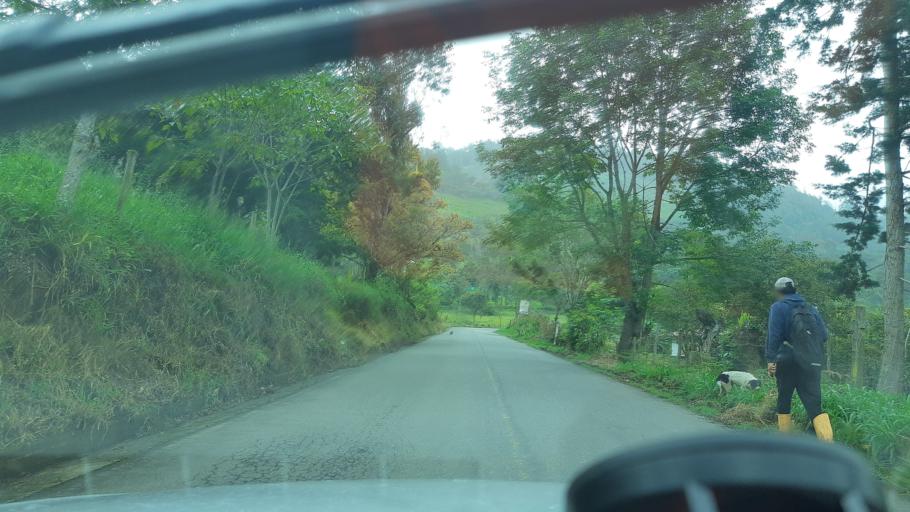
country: CO
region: Boyaca
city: Chinavita
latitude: 5.1706
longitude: -73.3763
